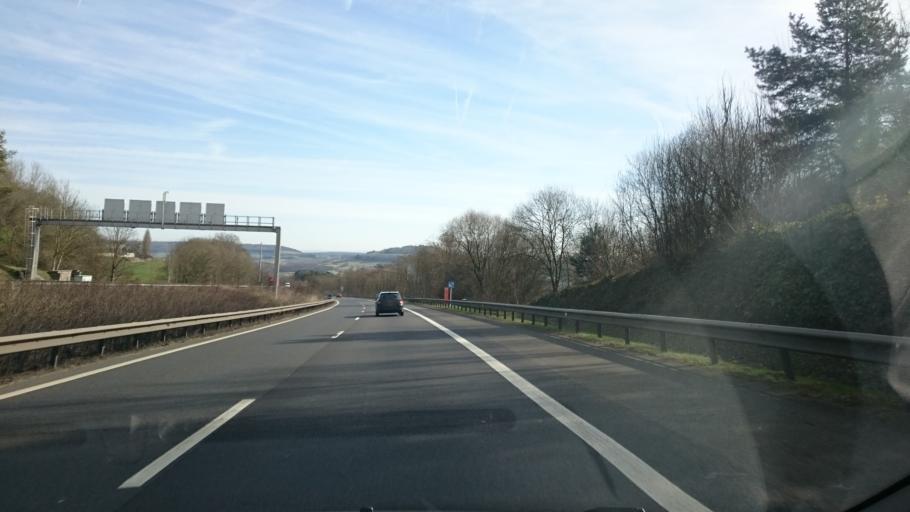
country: LU
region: Luxembourg
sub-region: Canton de Luxembourg
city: Niederanven
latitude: 49.6367
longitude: 6.2442
